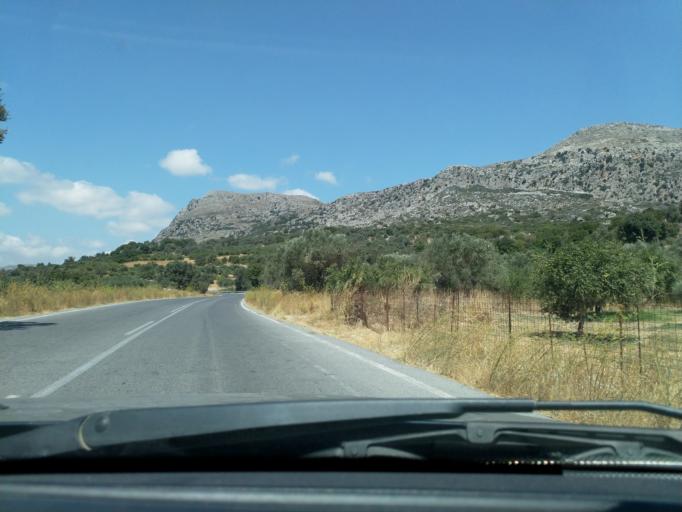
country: GR
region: Crete
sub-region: Nomos Rethymnis
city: Agia Foteini
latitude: 35.1924
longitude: 24.5518
